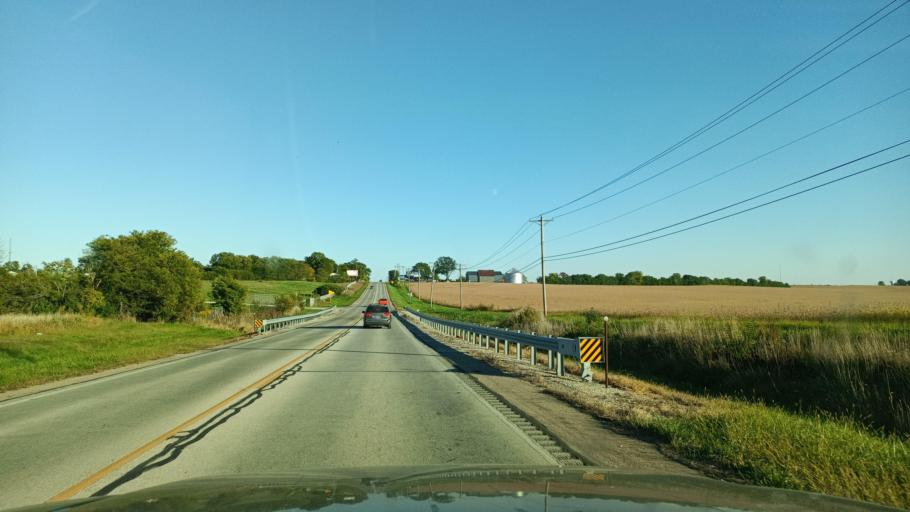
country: US
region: Illinois
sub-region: Champaign County
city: Lake of the Woods
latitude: 40.1584
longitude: -88.3111
